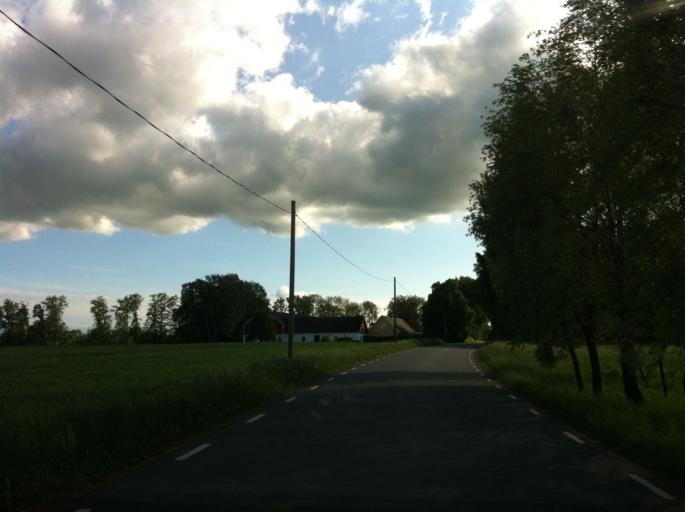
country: SE
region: Skane
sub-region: Svalovs Kommun
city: Kagerod
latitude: 56.0178
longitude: 13.1094
